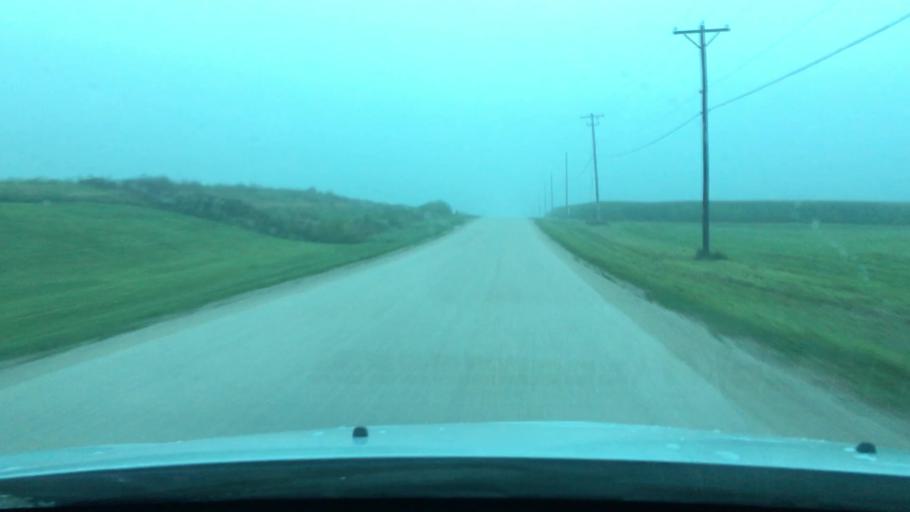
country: US
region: Illinois
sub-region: Ogle County
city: Rochelle
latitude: 41.9203
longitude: -88.9929
